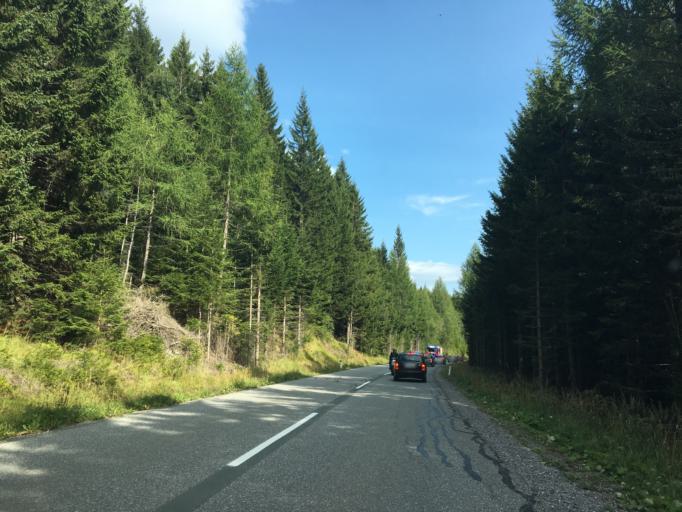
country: AT
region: Styria
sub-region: Politischer Bezirk Deutschlandsberg
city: Kloster
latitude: 46.8304
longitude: 15.0397
